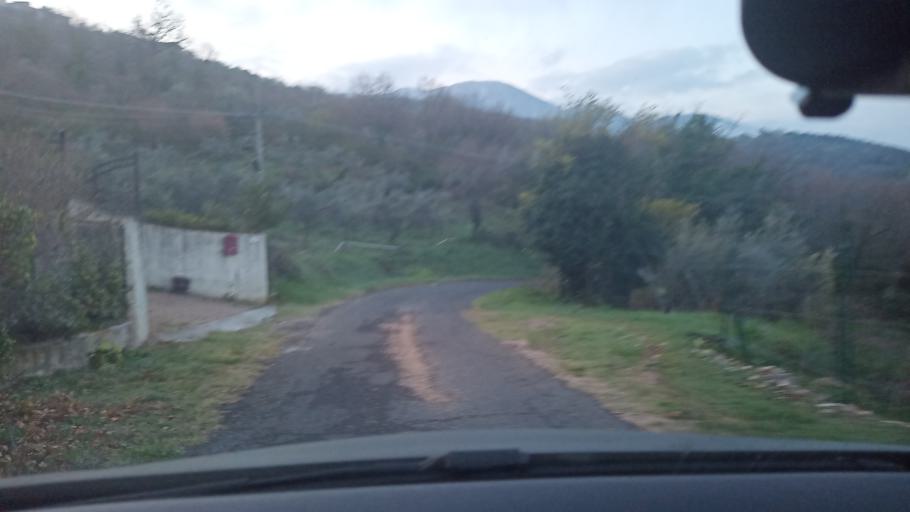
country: IT
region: Latium
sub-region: Provincia di Rieti
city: Cottanello
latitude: 42.4061
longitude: 12.6808
